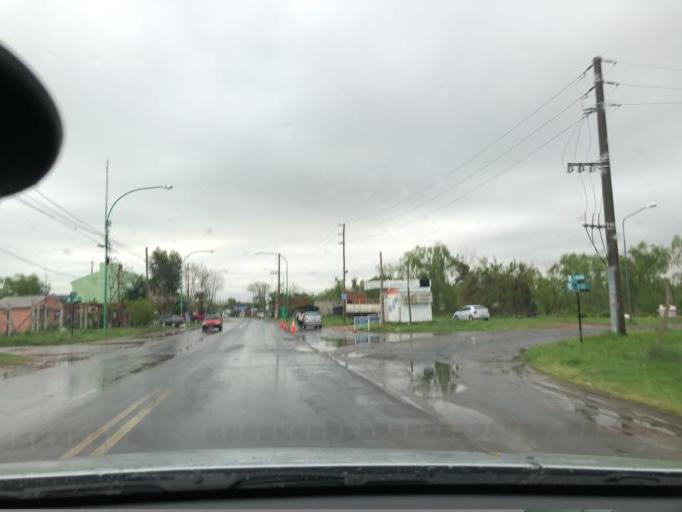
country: AR
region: Buenos Aires
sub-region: Partido de Ensenada
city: Ensenada
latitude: -34.8402
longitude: -57.9368
